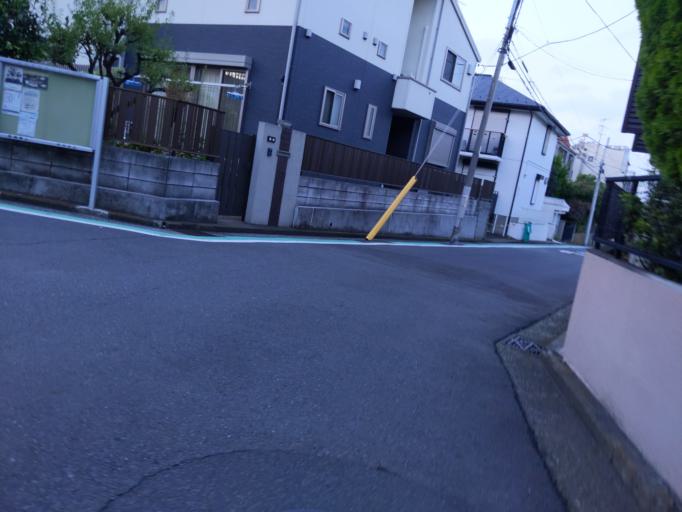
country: JP
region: Kanagawa
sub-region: Kawasaki-shi
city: Kawasaki
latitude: 35.5531
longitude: 139.6440
